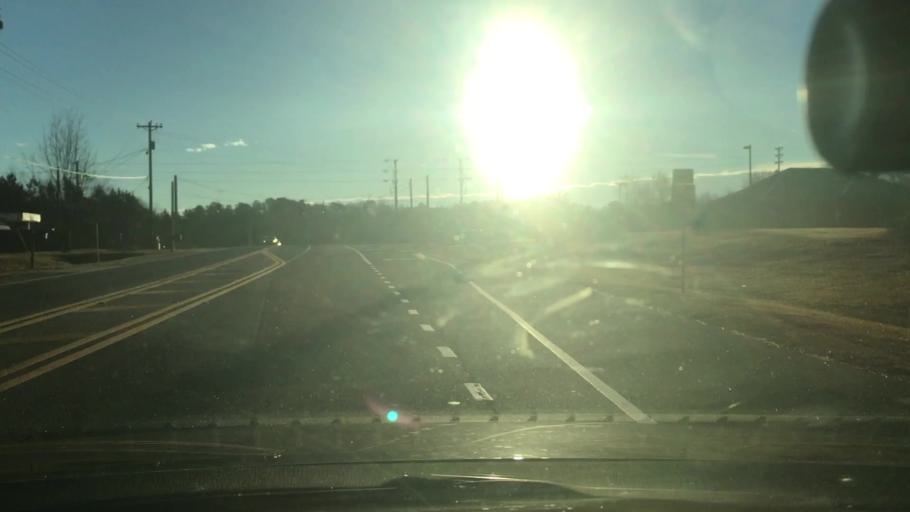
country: US
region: Georgia
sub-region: Fayette County
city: Peachtree City
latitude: 33.3419
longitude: -84.6471
